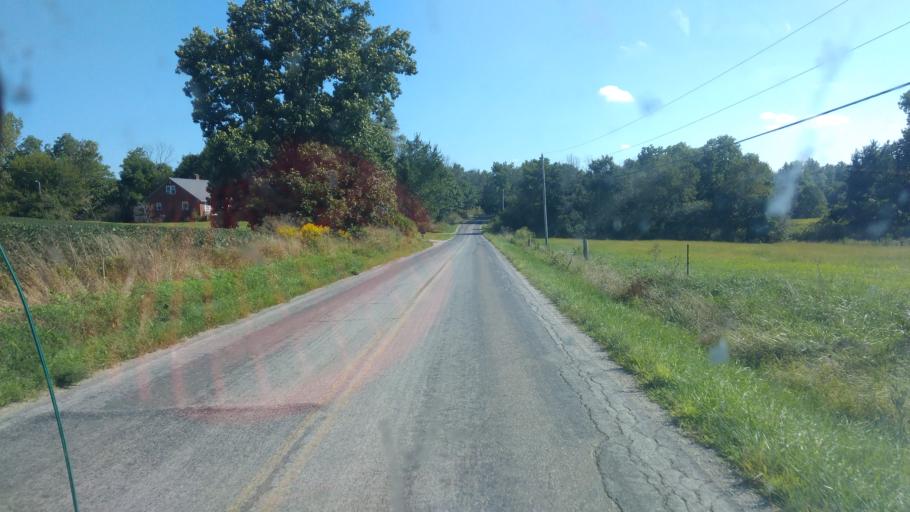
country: US
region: Ohio
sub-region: Ashland County
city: Ashland
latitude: 40.9129
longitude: -82.4359
